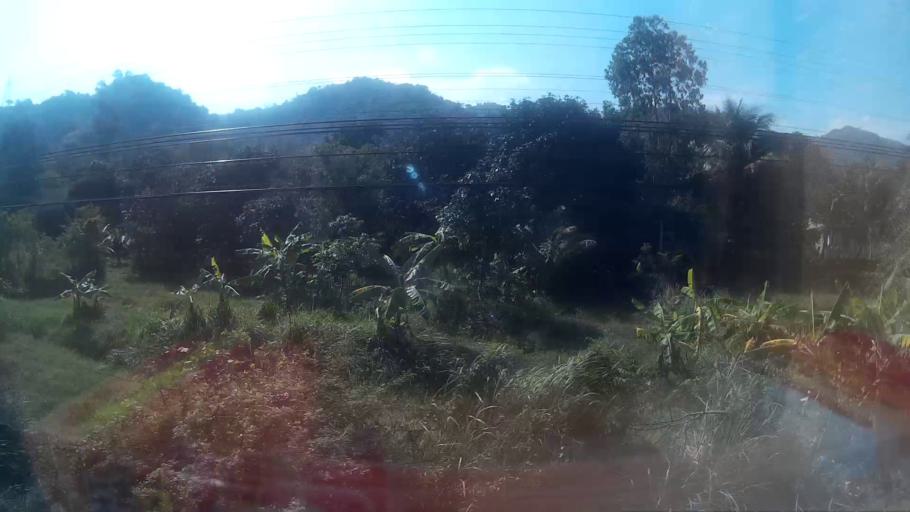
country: VN
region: Khanh Hoa
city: Ninh Hoa
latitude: 12.4246
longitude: 109.1392
